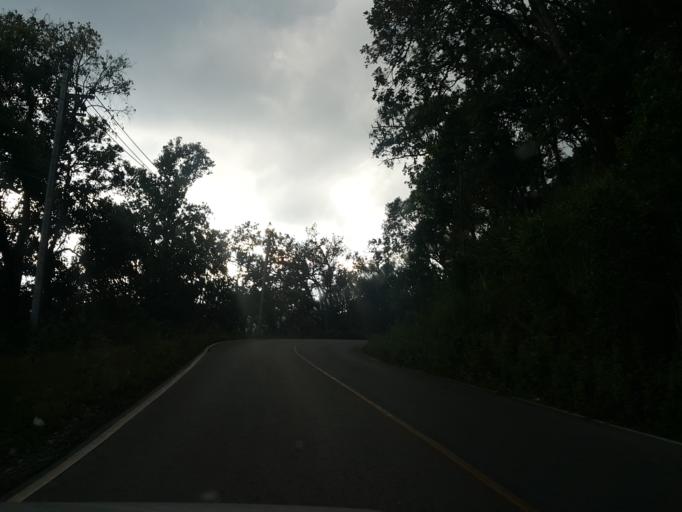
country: TH
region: Mae Hong Son
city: Khun Yuam
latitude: 18.7648
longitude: 98.1747
